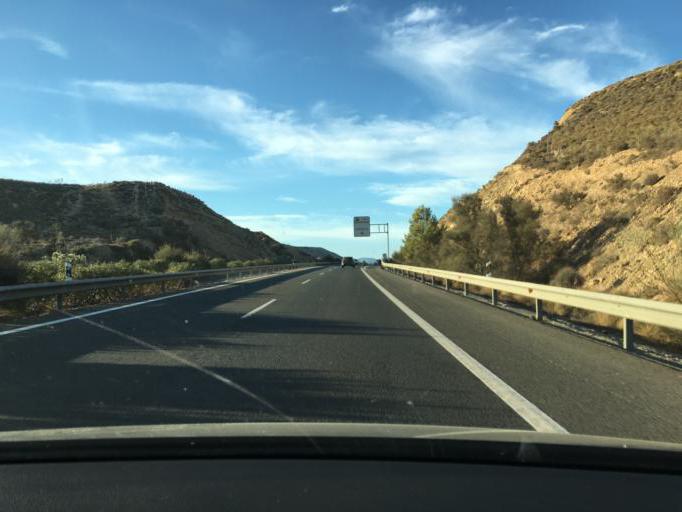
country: ES
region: Andalusia
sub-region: Provincia de Almeria
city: Sorbas
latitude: 37.0617
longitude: -2.0527
